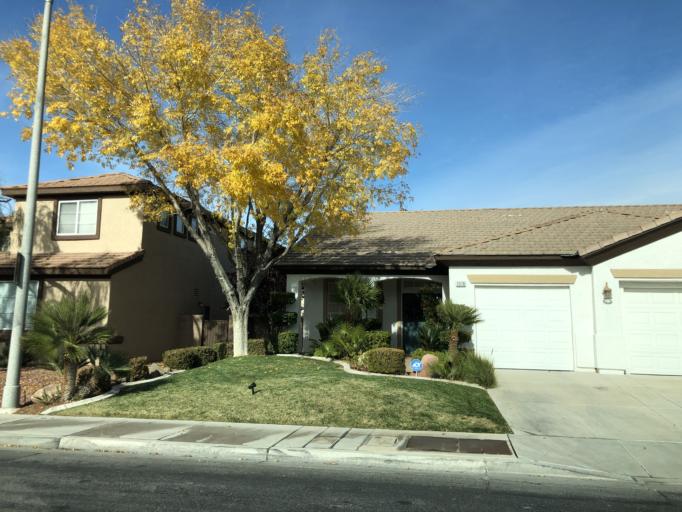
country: US
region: Nevada
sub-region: Clark County
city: Whitney
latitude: 36.0091
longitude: -115.0940
